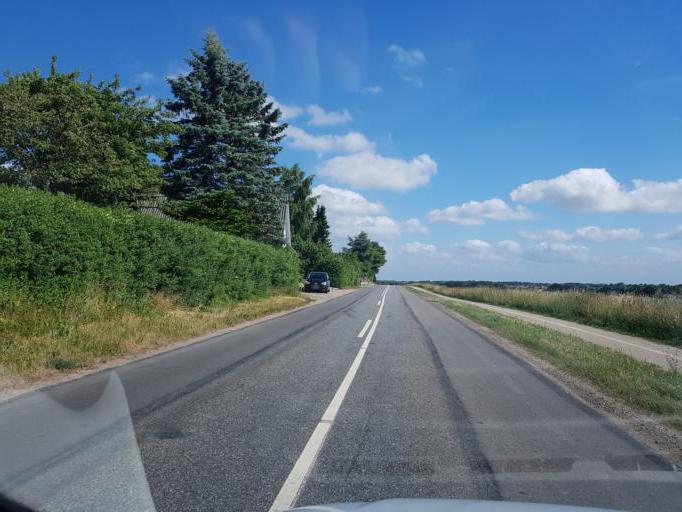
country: DK
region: Zealand
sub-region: Lejre Kommune
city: Osted
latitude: 55.5778
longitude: 11.9670
